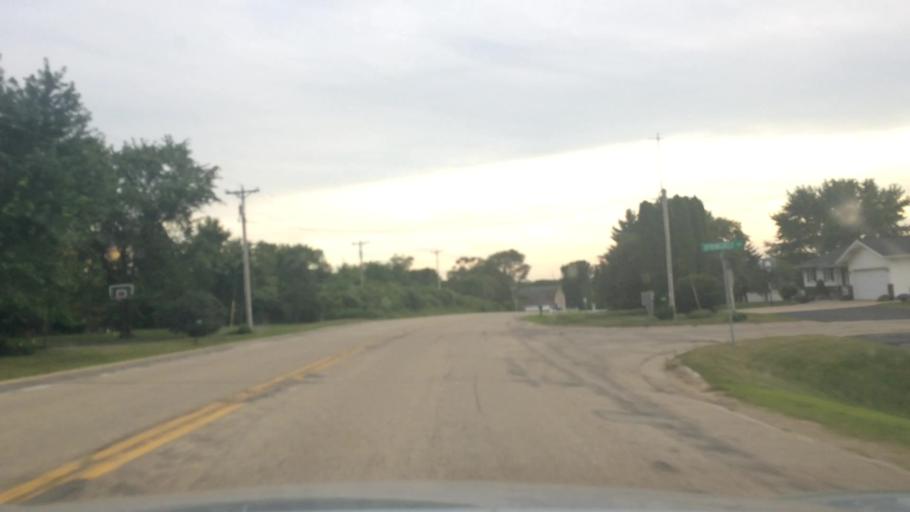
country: US
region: Wisconsin
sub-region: Dane County
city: Waunakee
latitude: 43.1994
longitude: -89.5525
